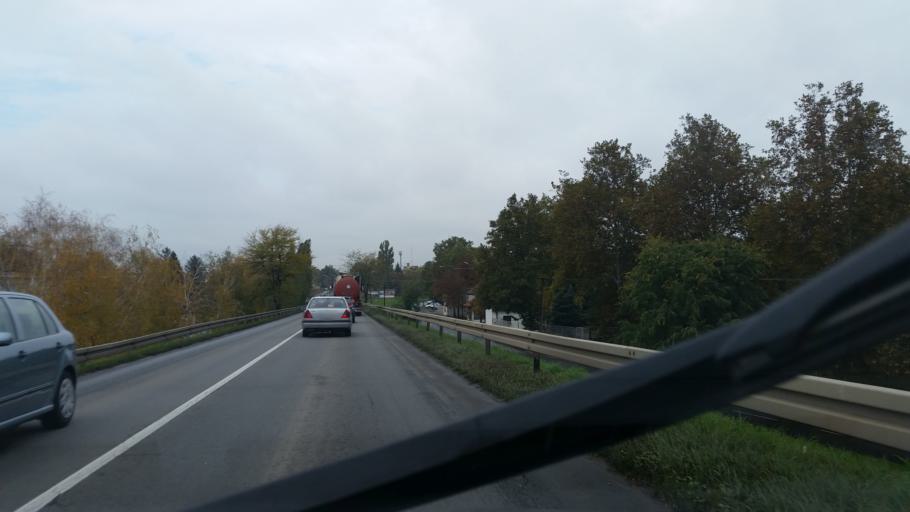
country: RS
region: Autonomna Pokrajina Vojvodina
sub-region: Srednjebanatski Okrug
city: Zrenjanin
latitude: 45.3709
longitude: 20.4186
